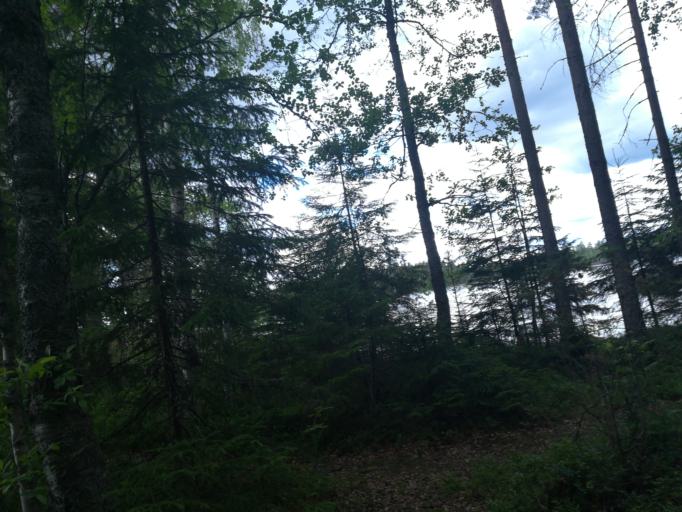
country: FI
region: Southern Savonia
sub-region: Mikkeli
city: Mikkeli
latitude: 61.6909
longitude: 27.0338
